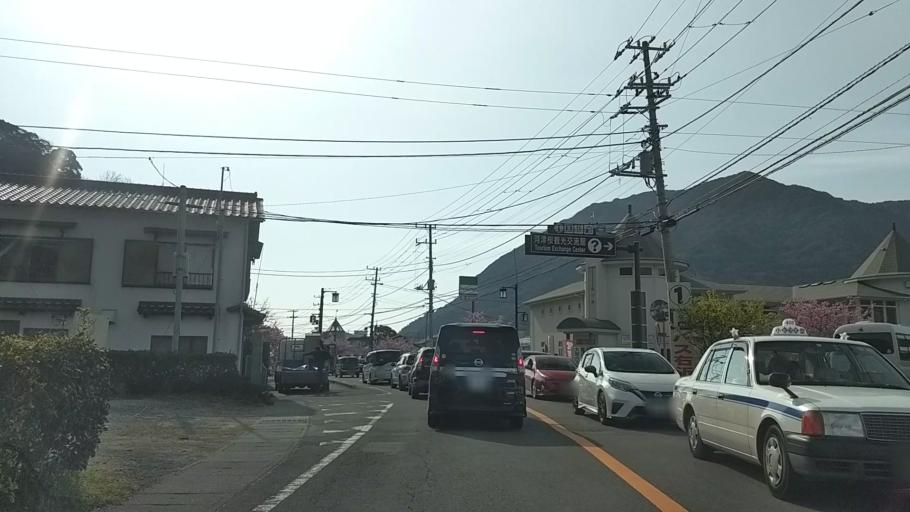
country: JP
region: Shizuoka
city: Shimoda
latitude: 34.7514
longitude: 138.9920
